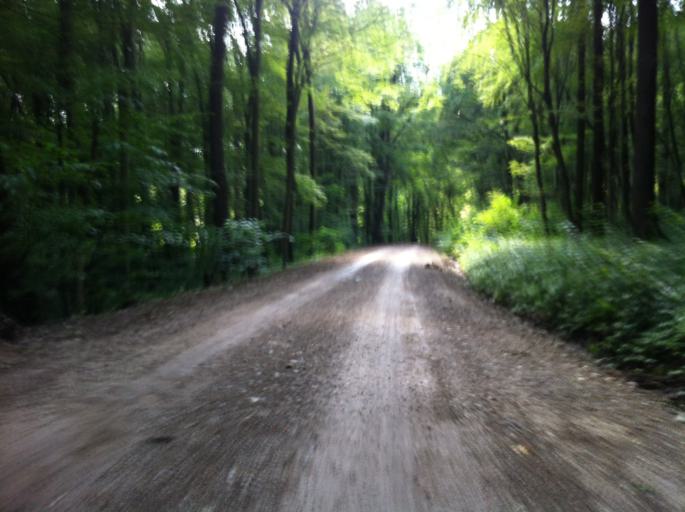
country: AT
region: Lower Austria
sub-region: Politischer Bezirk Modling
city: Laab im Walde
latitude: 48.1781
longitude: 16.1560
